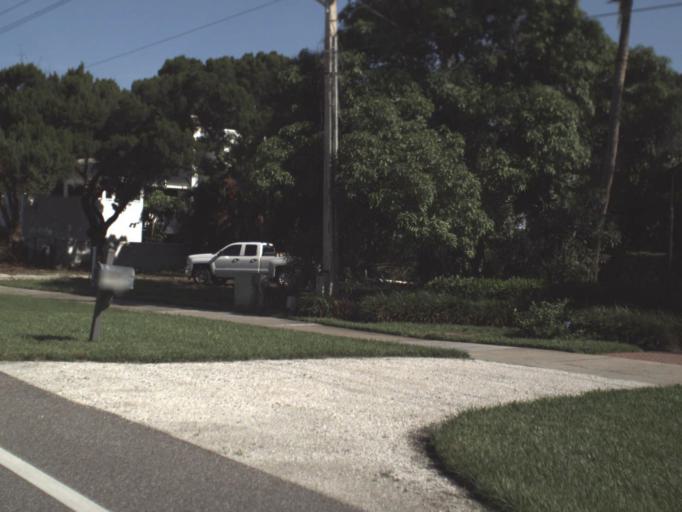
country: US
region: Florida
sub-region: Manatee County
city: Longboat Key
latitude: 27.4049
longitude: -82.6517
